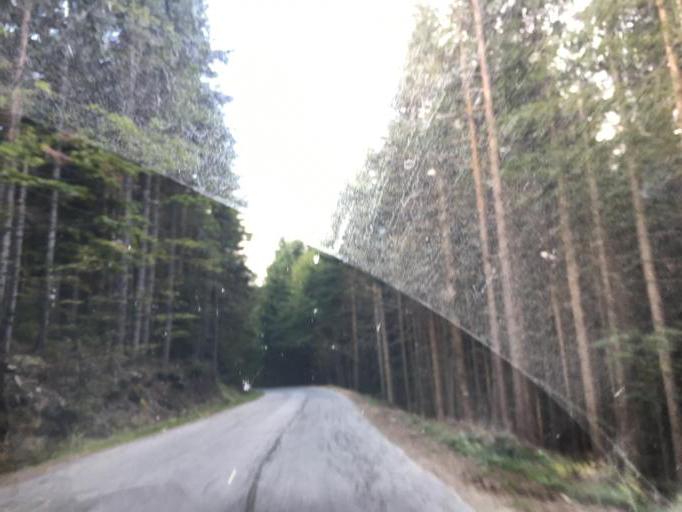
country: BG
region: Pazardzhik
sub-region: Obshtina Batak
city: Batak
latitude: 41.9201
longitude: 24.2839
